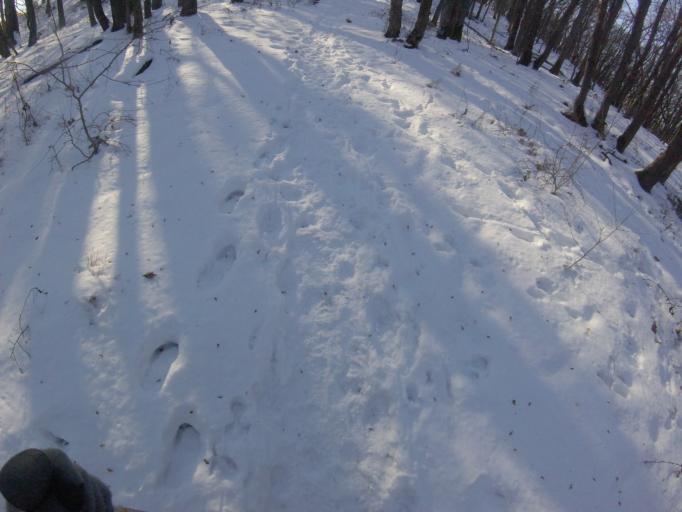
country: SK
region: Nitriansky
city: Sahy
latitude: 47.9840
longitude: 18.8887
